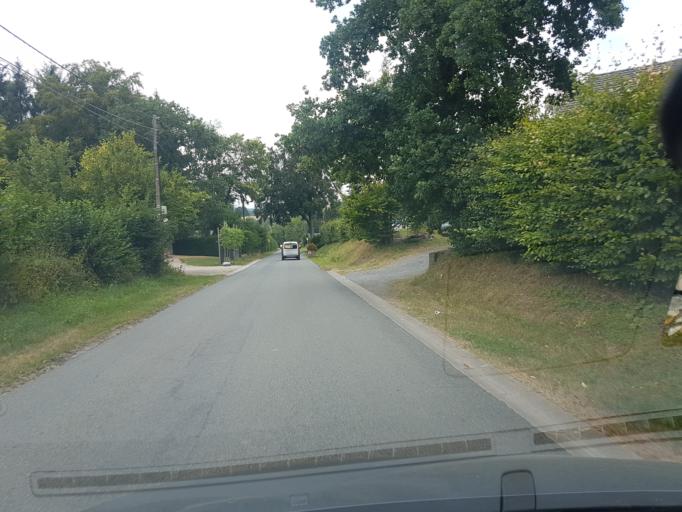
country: BE
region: Wallonia
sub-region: Province du Luxembourg
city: Manhay
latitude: 50.2592
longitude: 5.6512
